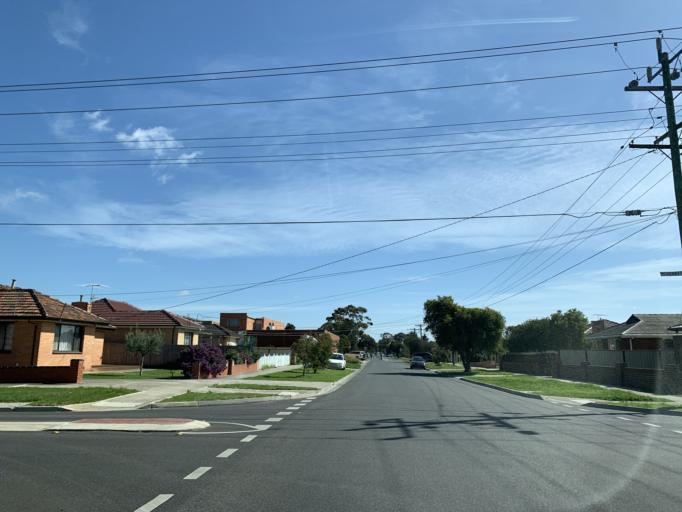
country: AU
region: Victoria
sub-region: Brimbank
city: Saint Albans
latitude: -37.7353
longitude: 144.8061
